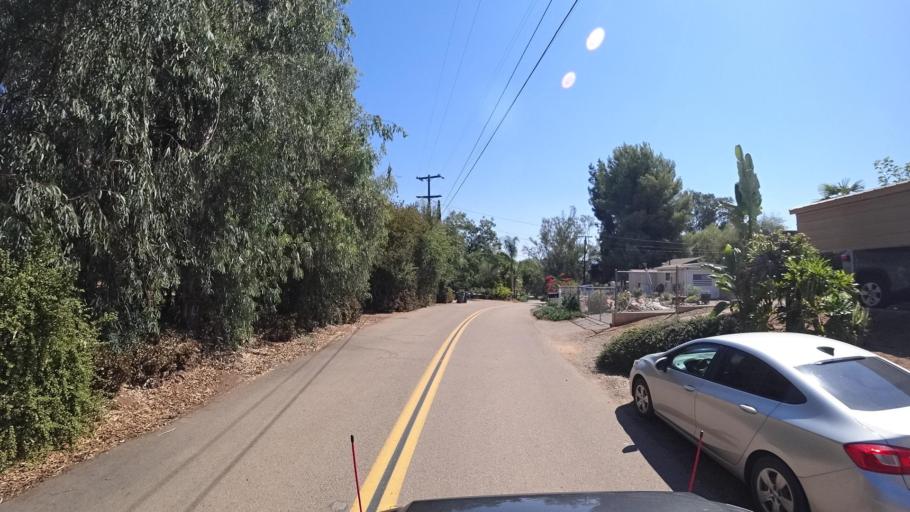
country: US
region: California
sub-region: San Diego County
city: Crest
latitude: 32.8023
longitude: -116.8690
